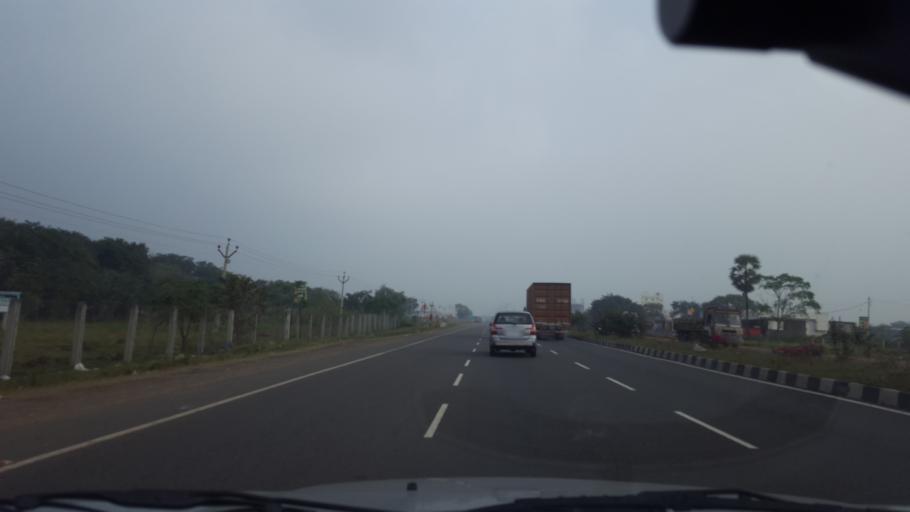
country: IN
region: Andhra Pradesh
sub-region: Prakasam
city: Addanki
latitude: 15.6805
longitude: 80.0173
